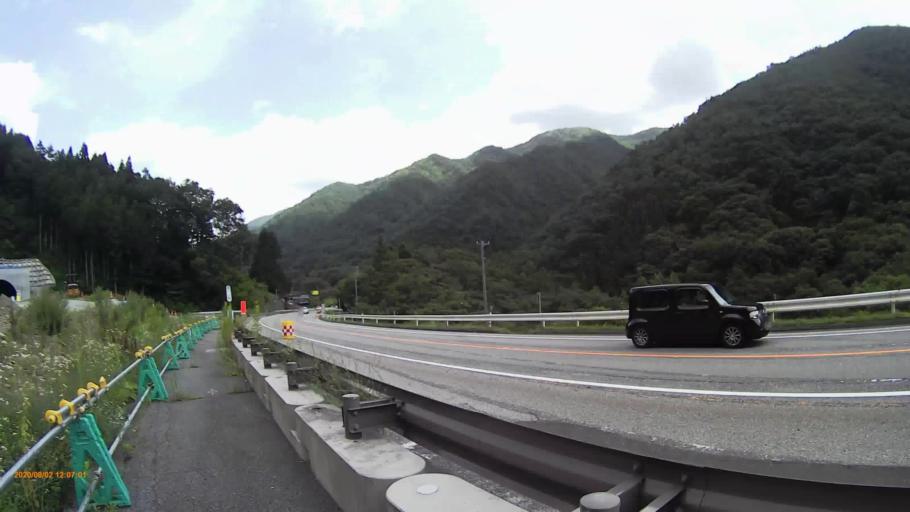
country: JP
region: Nagano
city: Shiojiri
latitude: 36.0273
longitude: 137.8716
